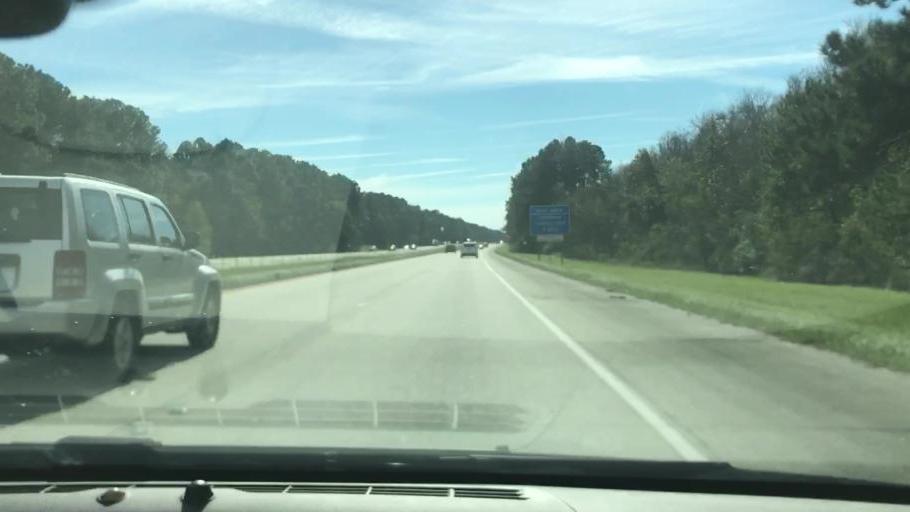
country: US
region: Louisiana
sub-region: Saint Tammany Parish
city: Pearl River
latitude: 30.3390
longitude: -89.7383
